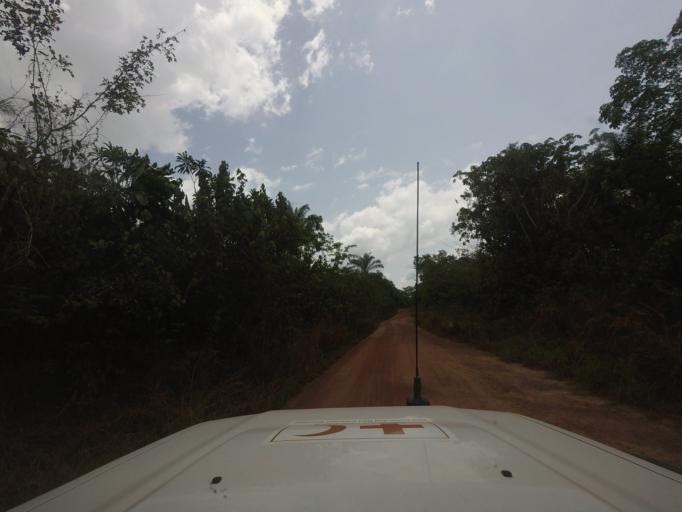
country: LR
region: Bong
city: Gbarnga
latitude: 7.1083
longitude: -9.2256
